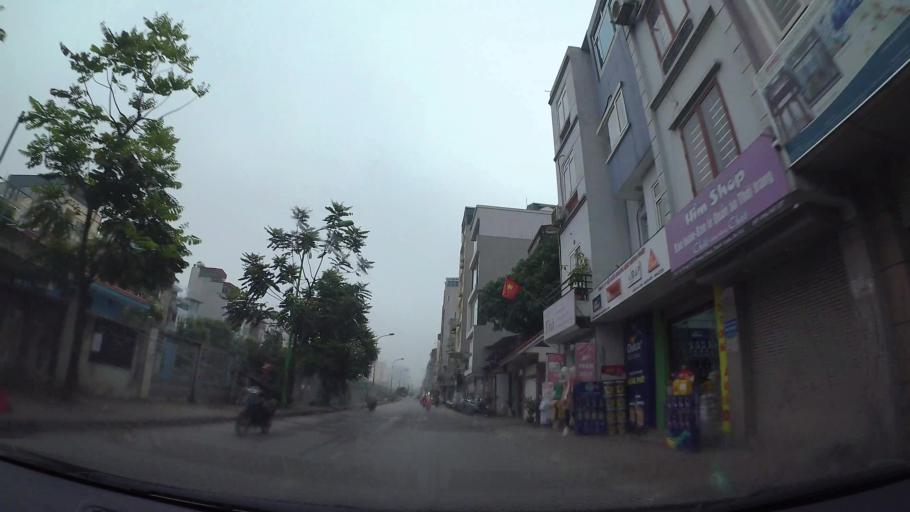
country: VN
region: Ha Noi
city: Hai BaTrung
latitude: 20.9941
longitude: 105.8364
